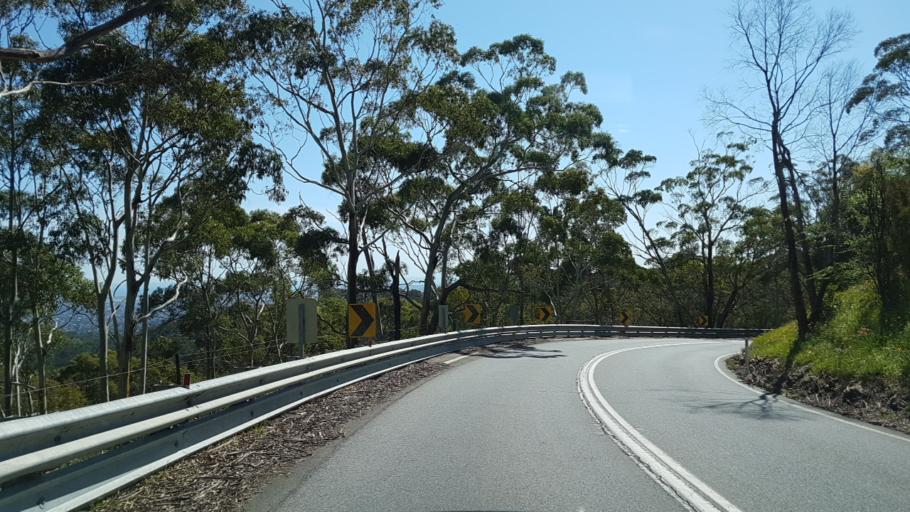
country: AU
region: South Australia
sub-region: Burnside
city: Beaumont
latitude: -34.9539
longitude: 138.6961
